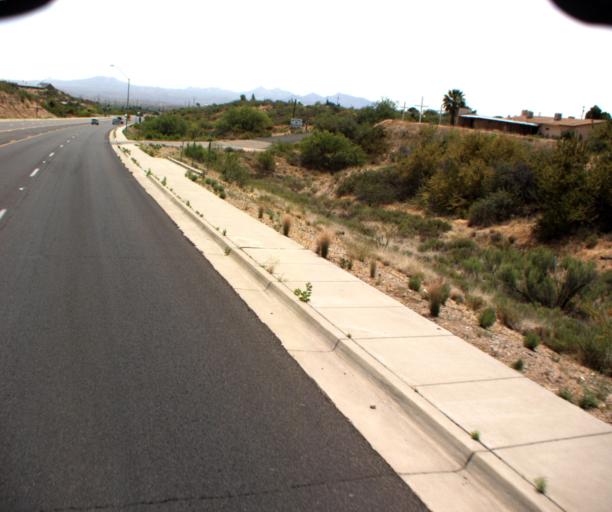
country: US
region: Arizona
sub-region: Gila County
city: Globe
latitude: 33.3813
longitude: -110.7519
